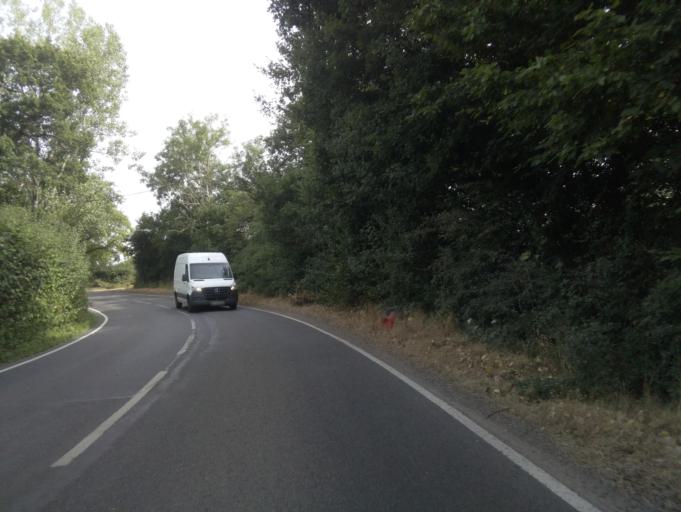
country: GB
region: England
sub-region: Surrey
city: Godstone
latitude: 51.1958
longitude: -0.0644
